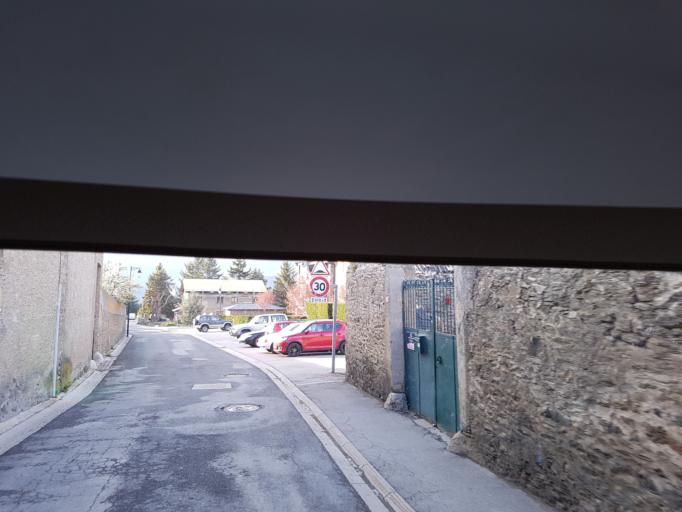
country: FR
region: Languedoc-Roussillon
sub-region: Departement des Pyrenees-Orientales
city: Osseja
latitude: 42.4389
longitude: 2.0367
